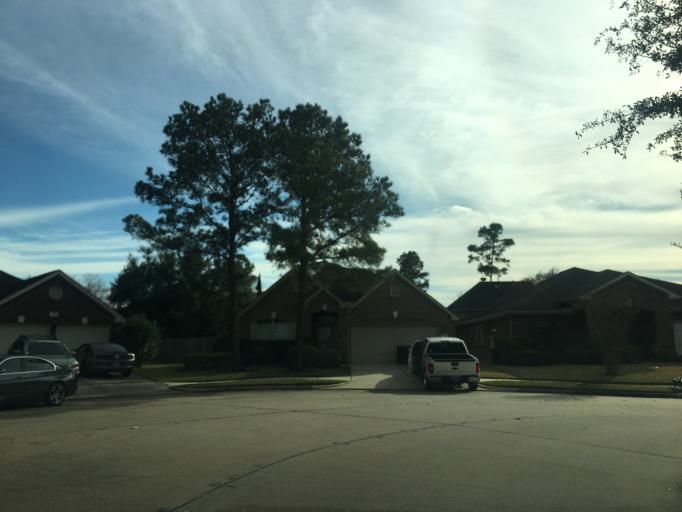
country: US
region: Texas
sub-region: Harris County
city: Cloverleaf
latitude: 29.8122
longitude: -95.1679
